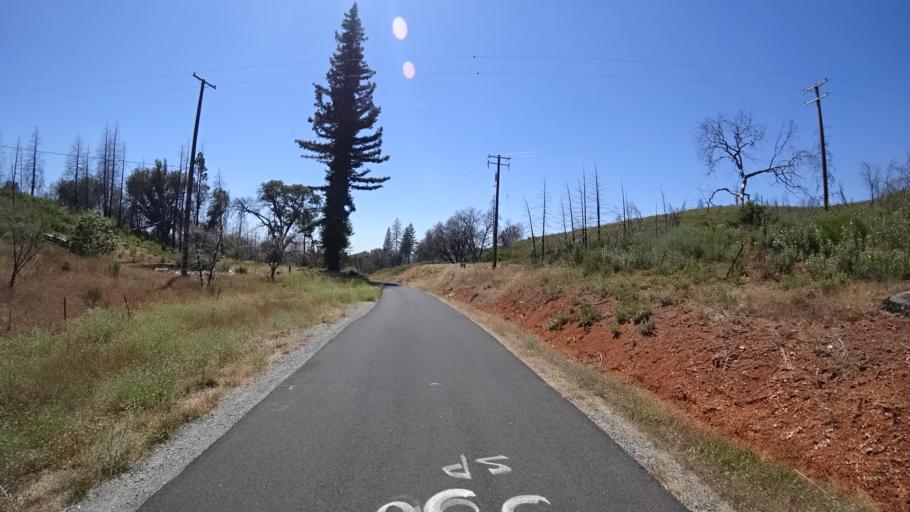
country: US
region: California
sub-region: Calaveras County
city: Mountain Ranch
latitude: 38.2748
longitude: -120.5566
